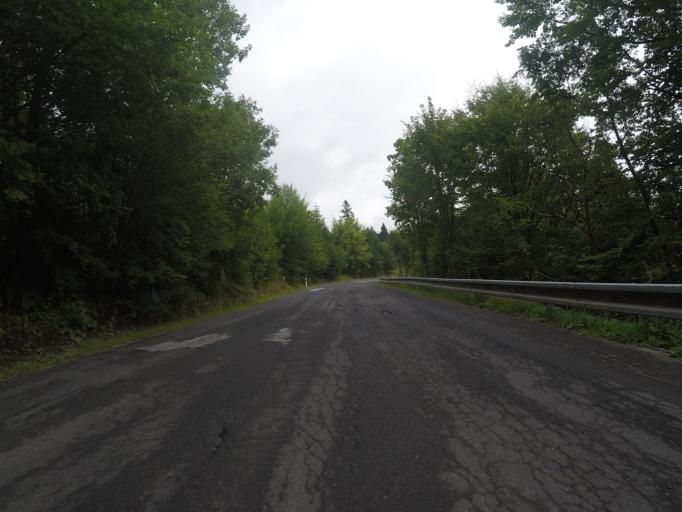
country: SK
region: Kosicky
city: Spisska Nova Ves
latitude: 48.8615
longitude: 20.5236
